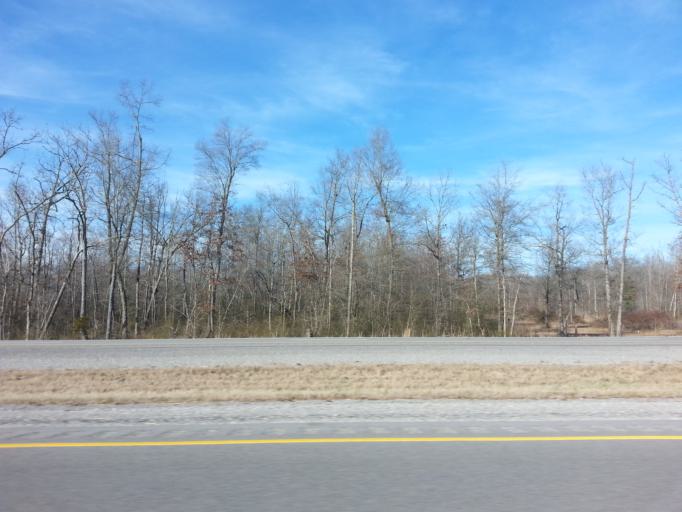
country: US
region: Tennessee
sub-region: Warren County
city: McMinnville
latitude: 35.7170
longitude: -85.8638
